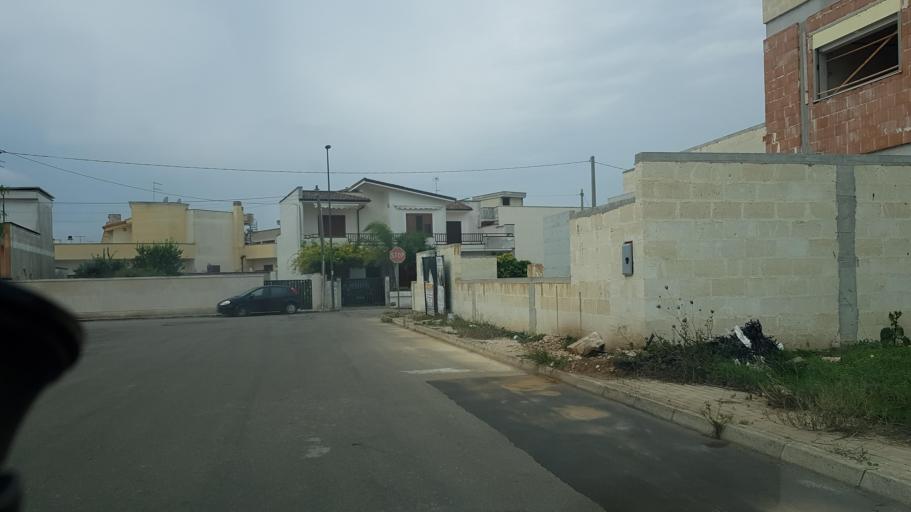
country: IT
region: Apulia
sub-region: Provincia di Lecce
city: Guagnano
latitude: 40.4056
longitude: 17.9508
